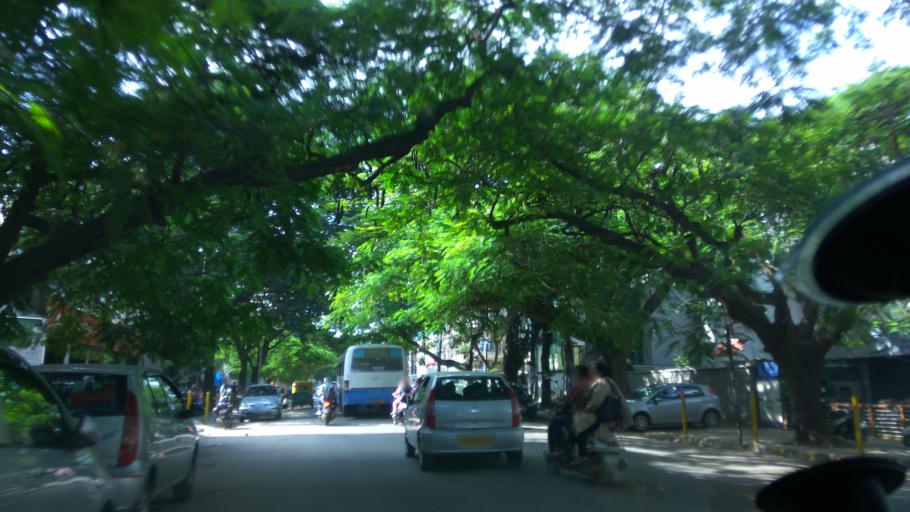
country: IN
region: Karnataka
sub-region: Bangalore Urban
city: Bangalore
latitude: 12.9710
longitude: 77.6473
